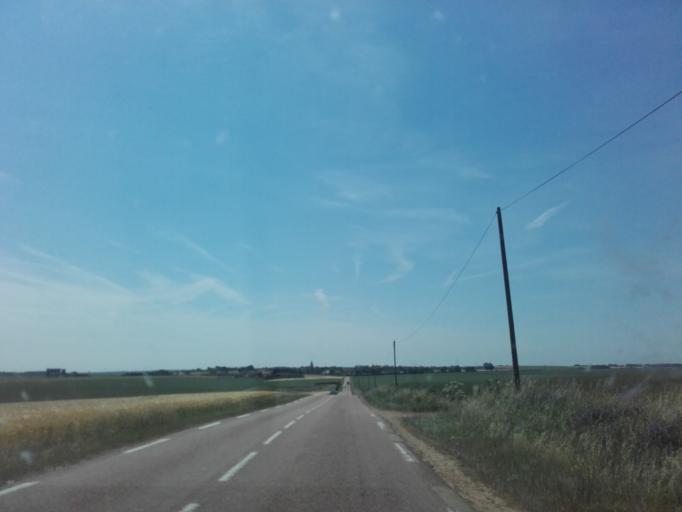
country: FR
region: Bourgogne
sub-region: Departement de l'Yonne
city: Joux-la-Ville
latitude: 47.6846
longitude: 3.8693
